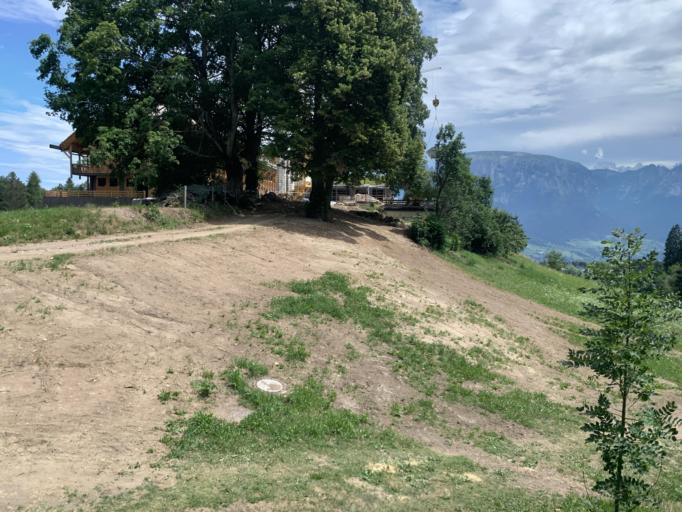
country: IT
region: Trentino-Alto Adige
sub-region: Bolzano
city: Renon - Ritten
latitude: 46.5320
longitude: 11.4388
